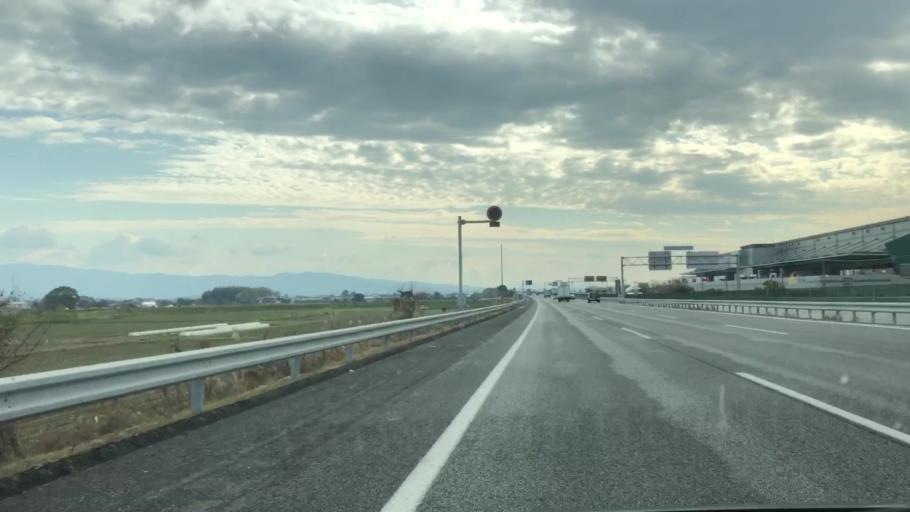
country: JP
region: Saga Prefecture
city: Tosu
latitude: 33.3902
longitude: 130.5384
